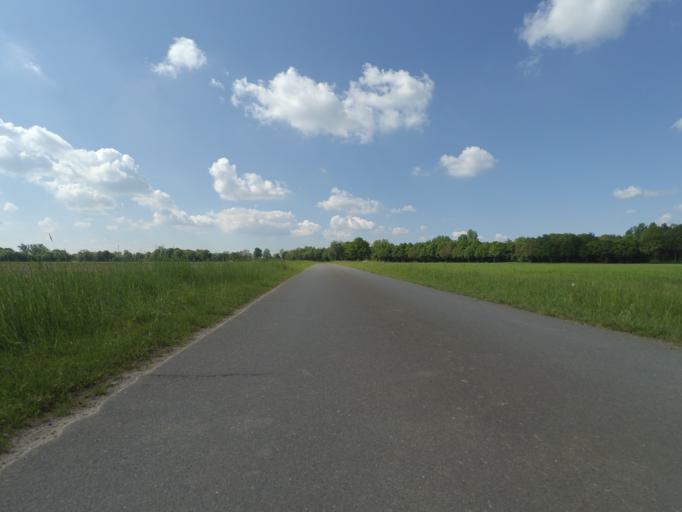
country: DE
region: Lower Saxony
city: Haenigsen
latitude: 52.5109
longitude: 10.0572
